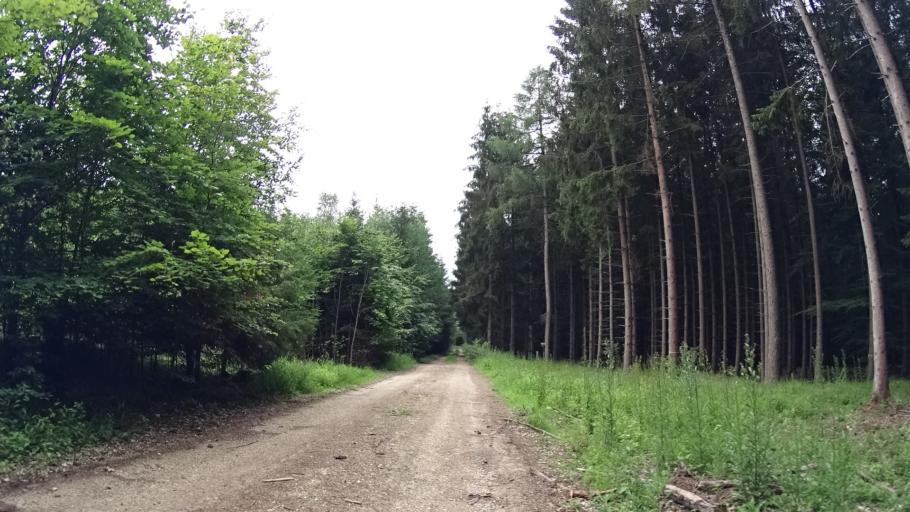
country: DE
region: Bavaria
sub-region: Upper Bavaria
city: Denkendorf
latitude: 48.8949
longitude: 11.4385
